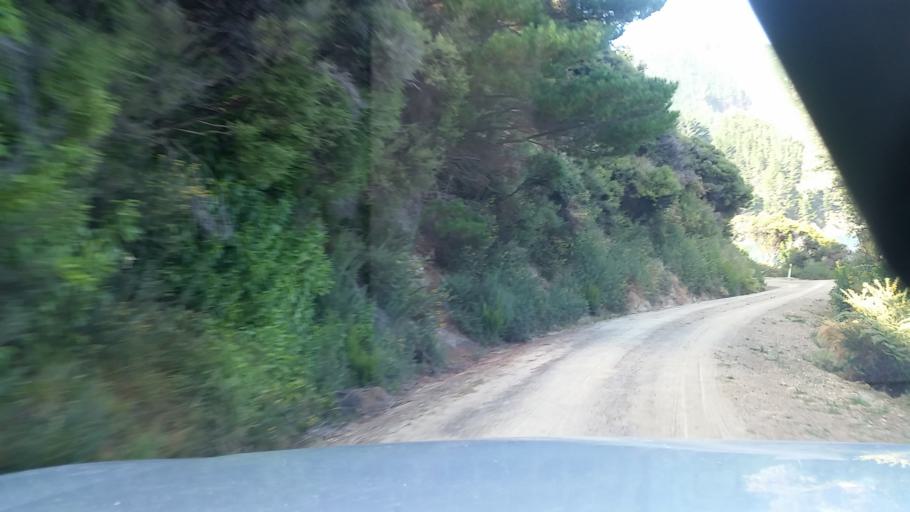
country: NZ
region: Marlborough
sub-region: Marlborough District
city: Picton
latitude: -41.3096
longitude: 174.1711
